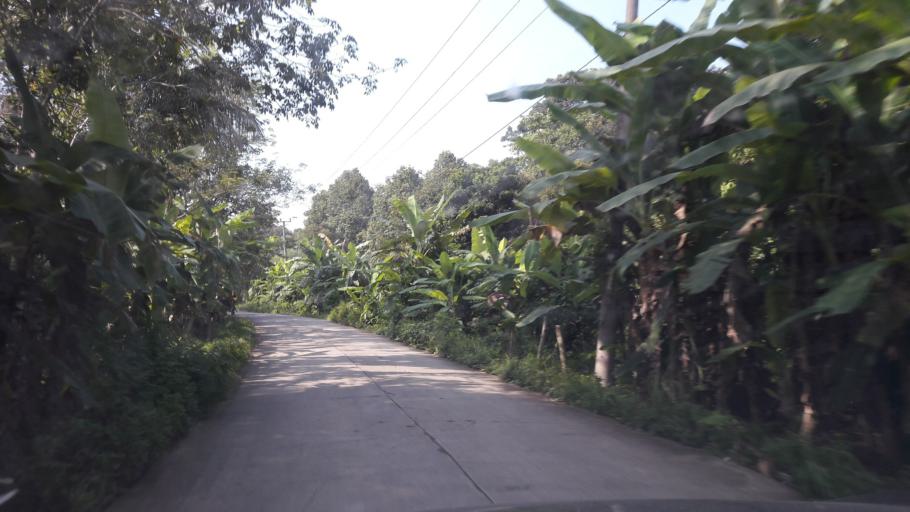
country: ID
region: South Sumatra
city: Prabumulih
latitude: -3.2833
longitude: 104.2185
